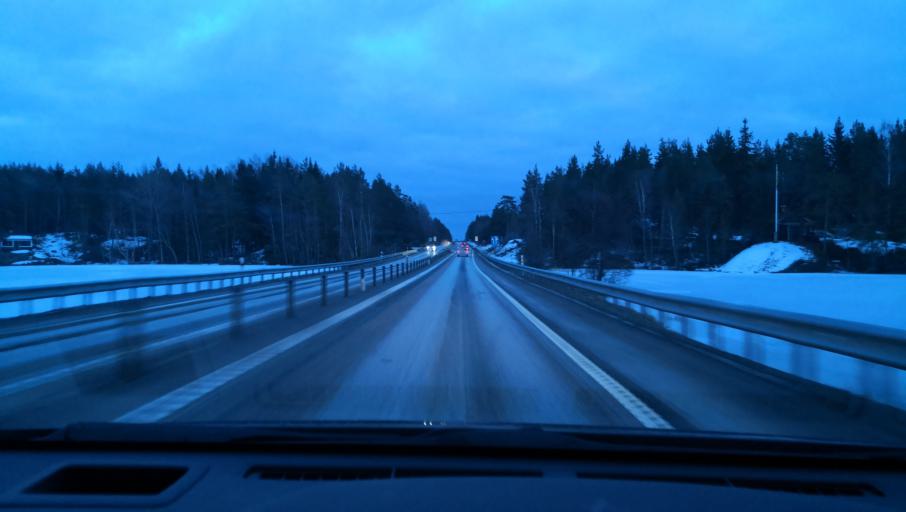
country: SE
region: Vaestmanland
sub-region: Surahammars Kommun
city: Surahammar
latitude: 59.6844
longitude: 16.2672
